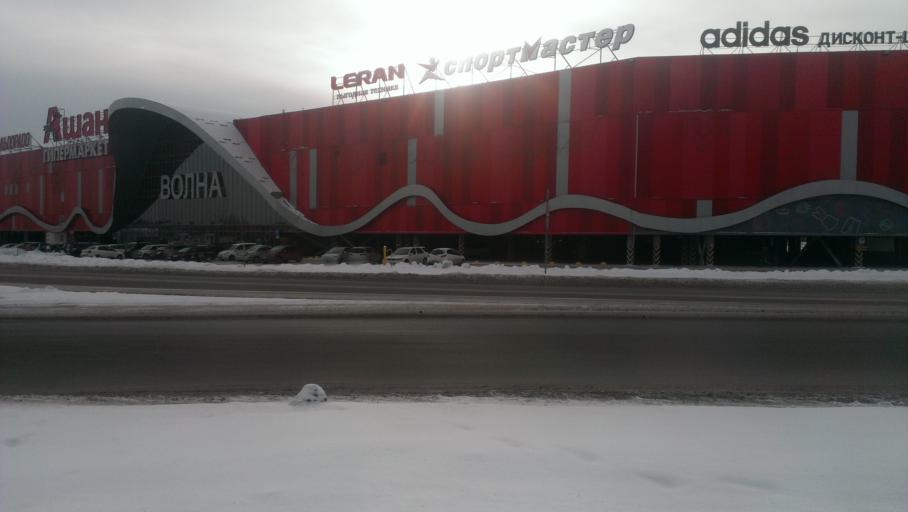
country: RU
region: Altai Krai
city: Novosilikatnyy
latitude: 53.3275
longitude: 83.6906
